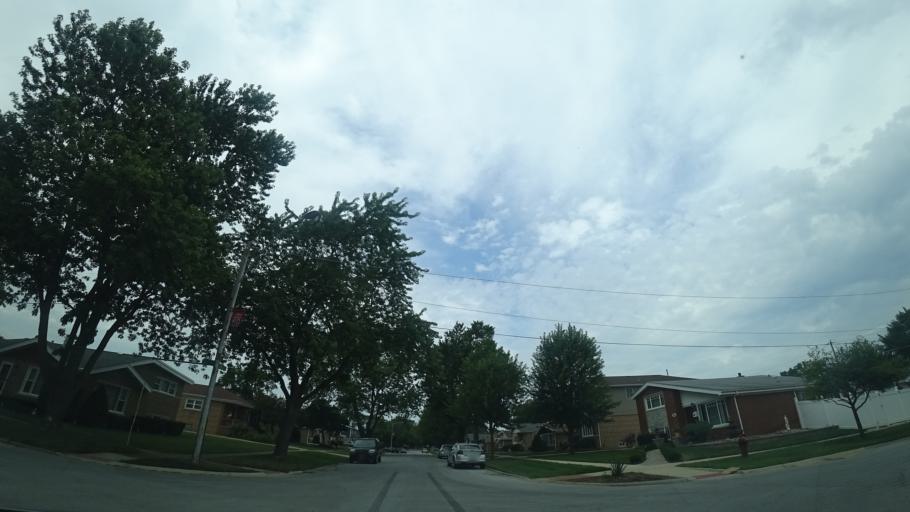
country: US
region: Illinois
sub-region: Cook County
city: Oak Lawn
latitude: 41.7000
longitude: -87.7317
